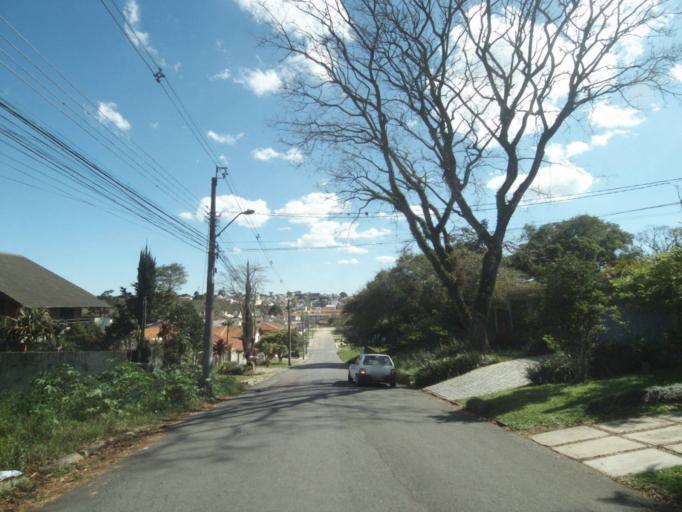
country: BR
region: Parana
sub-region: Curitiba
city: Curitiba
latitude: -25.3810
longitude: -49.2453
